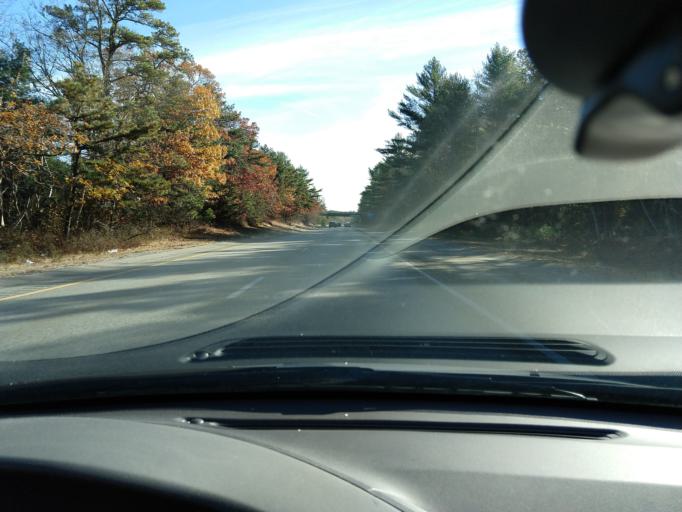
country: US
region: Massachusetts
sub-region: Plymouth County
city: White Island Shores
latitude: 41.8605
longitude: -70.5875
